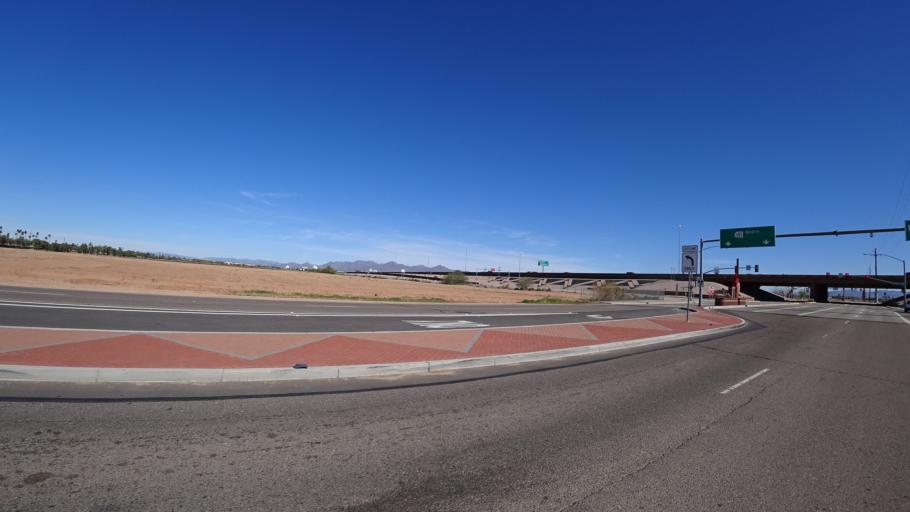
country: US
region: Arizona
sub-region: Maricopa County
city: Scottsdale
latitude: 33.4948
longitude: -111.8896
